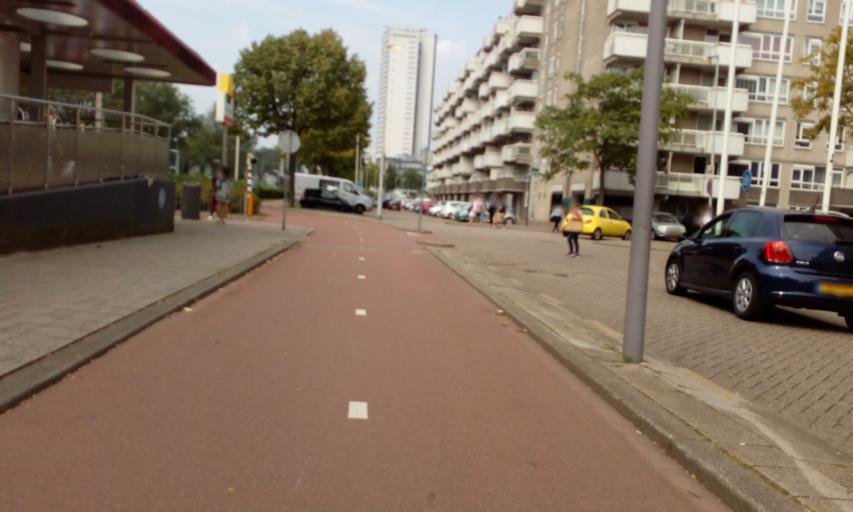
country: NL
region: South Holland
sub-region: Gemeente Rotterdam
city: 's-Gravenland
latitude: 51.9463
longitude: 4.5545
